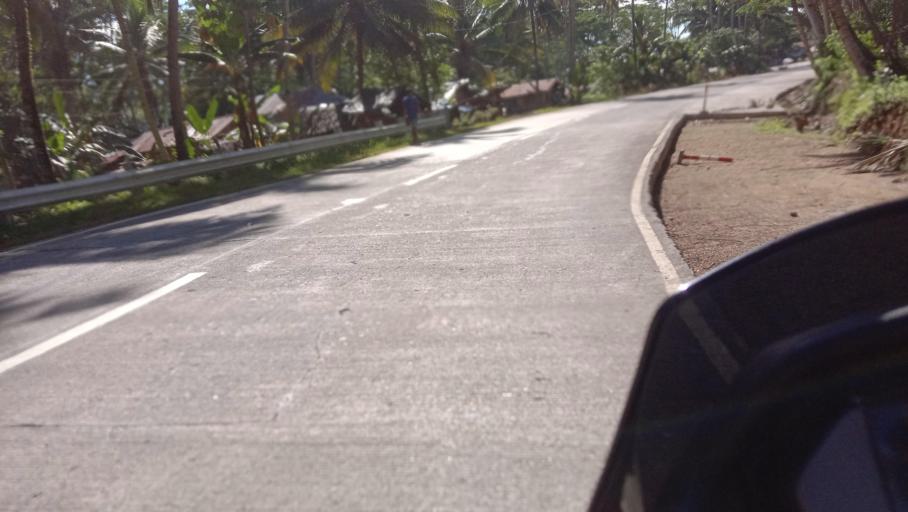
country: PH
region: Caraga
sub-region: Province of Surigao del Sur
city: Amaga
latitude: 8.5368
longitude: 126.0896
